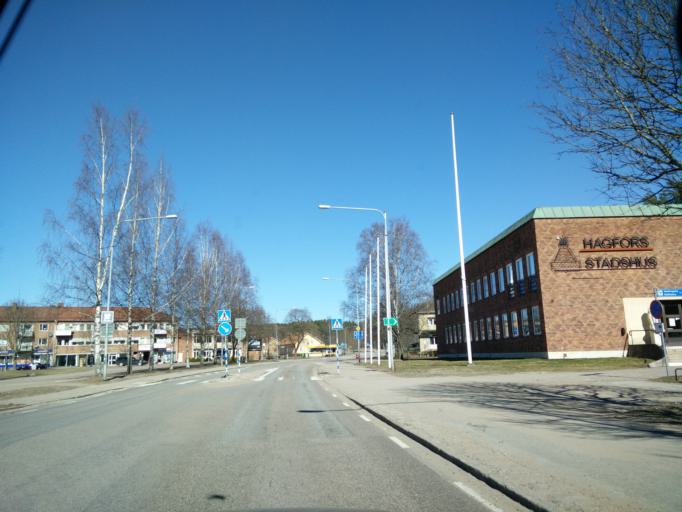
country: SE
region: Vaermland
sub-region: Hagfors Kommun
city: Hagfors
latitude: 60.0312
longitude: 13.7013
